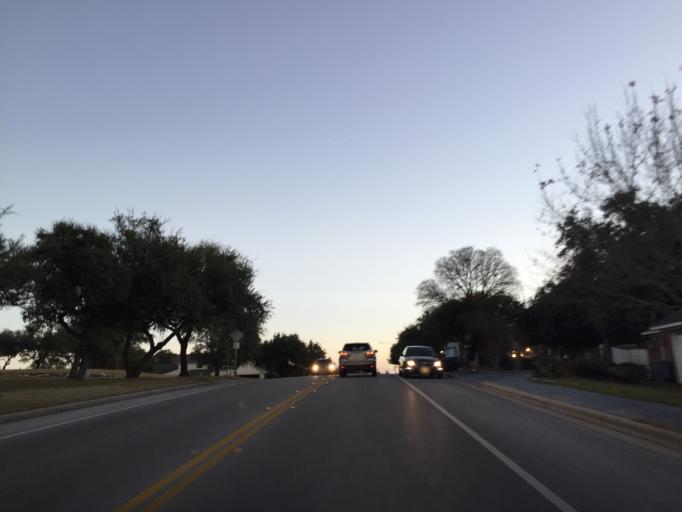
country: US
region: Texas
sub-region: Williamson County
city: Jollyville
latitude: 30.4081
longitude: -97.7700
